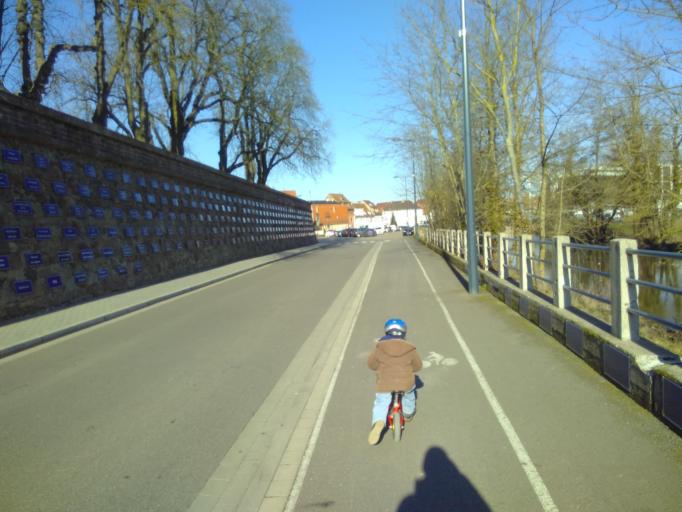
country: FR
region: Alsace
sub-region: Departement du Bas-Rhin
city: Selestat
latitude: 48.2545
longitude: 7.4540
